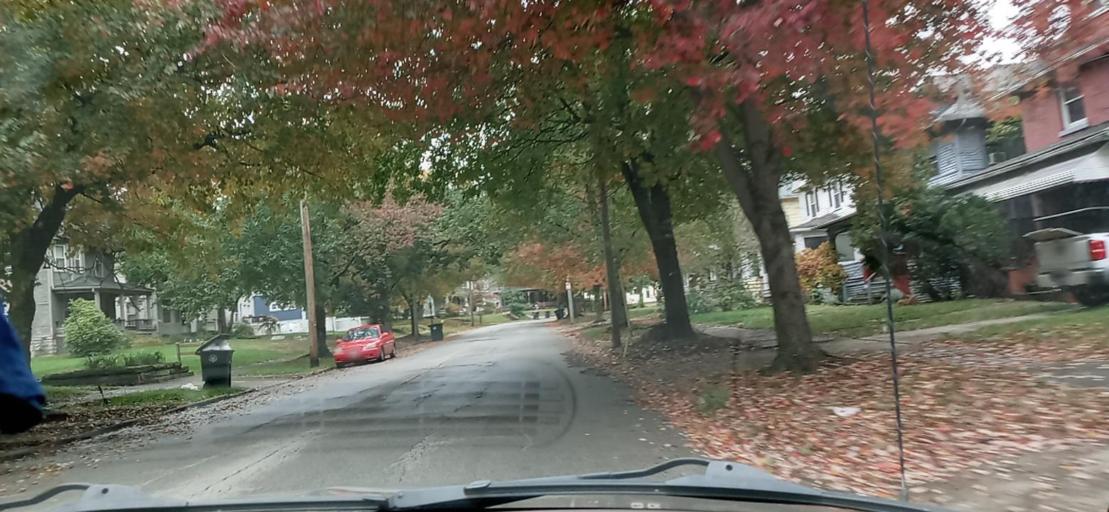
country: US
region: Ohio
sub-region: Summit County
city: Akron
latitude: 41.0885
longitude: -81.5349
